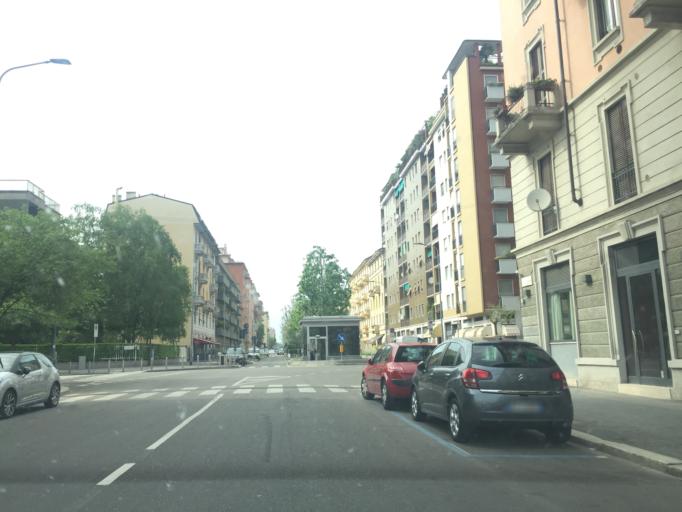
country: IT
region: Lombardy
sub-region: Citta metropolitana di Milano
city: Milano
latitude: 45.4886
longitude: 9.1684
